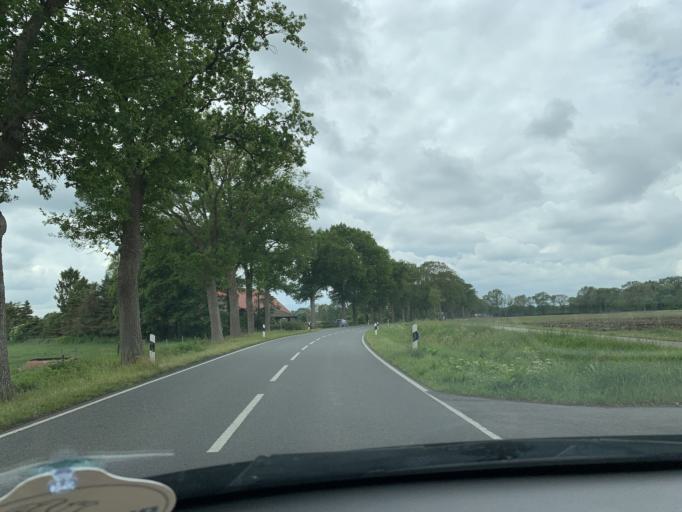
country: DE
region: Lower Saxony
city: Westerstede
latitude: 53.2974
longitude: 7.9945
